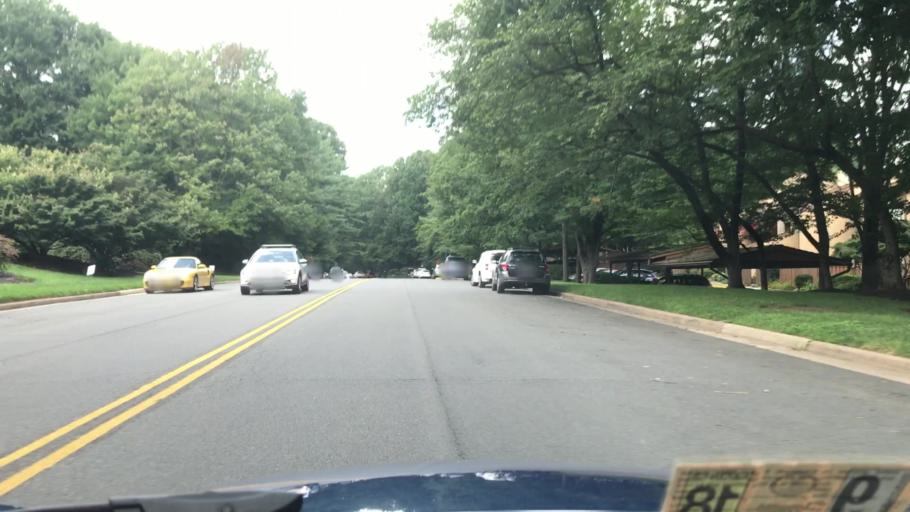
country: US
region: Virginia
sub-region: Fairfax County
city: Reston
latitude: 38.9348
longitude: -77.3338
